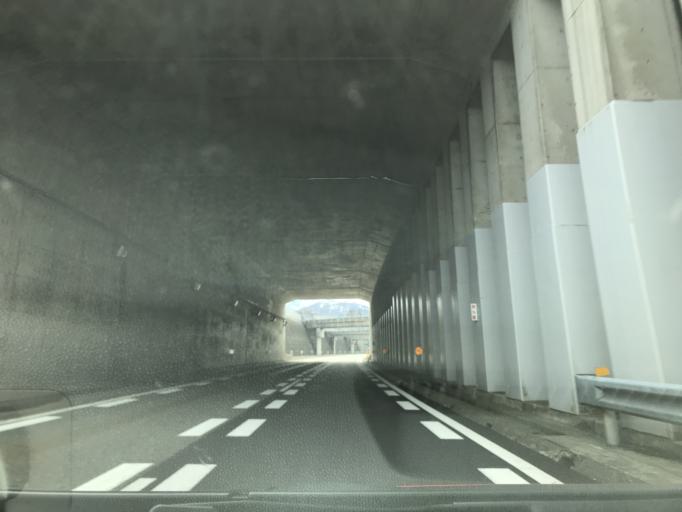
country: JP
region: Niigata
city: Ojiya
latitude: 37.2338
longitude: 138.9752
